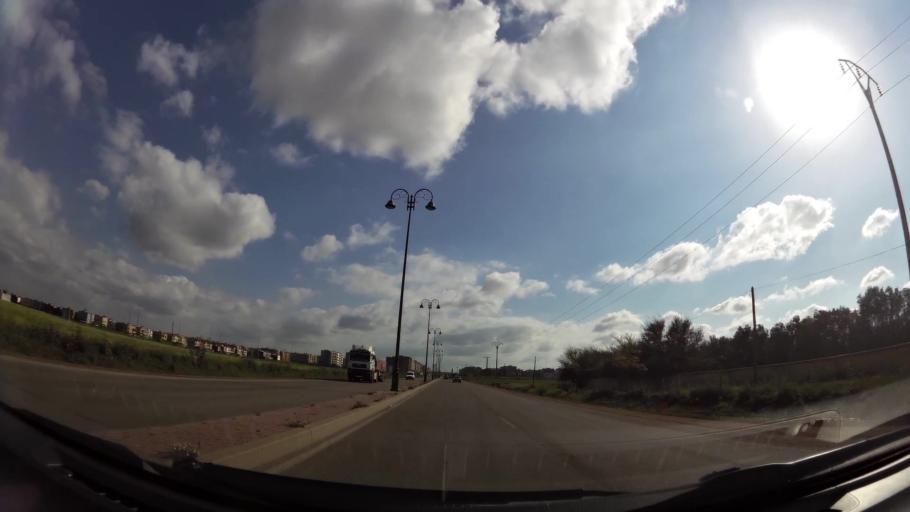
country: MA
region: Chaouia-Ouardigha
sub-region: Settat Province
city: Berrechid
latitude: 33.2832
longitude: -7.5788
